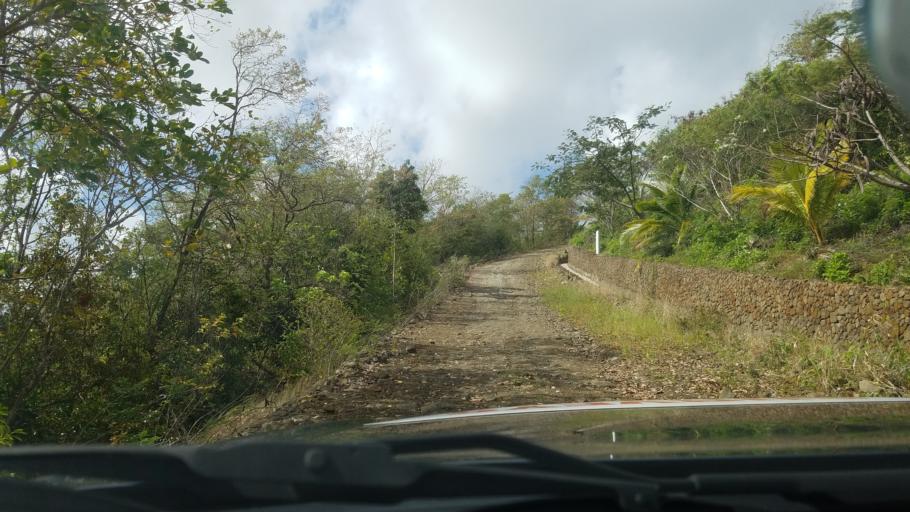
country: LC
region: Gros-Islet
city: Gros Islet
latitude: 14.0652
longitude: -60.9470
